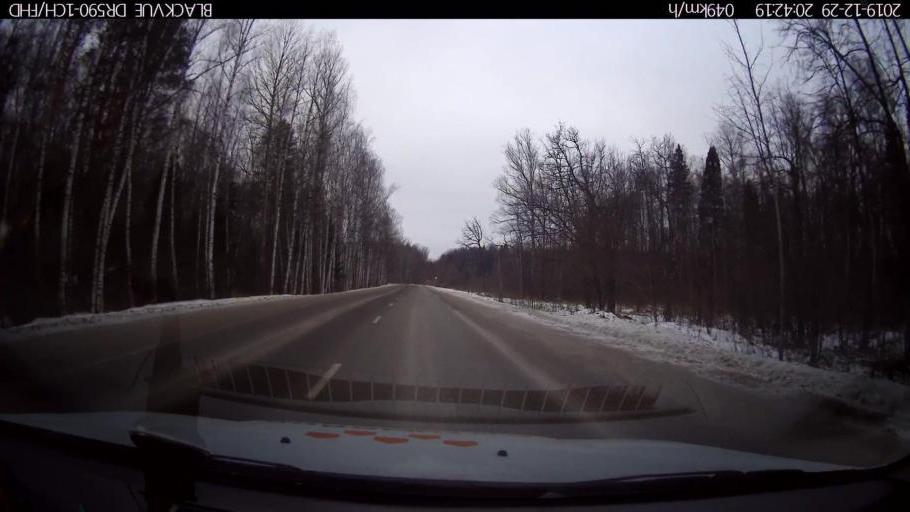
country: RU
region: Nizjnij Novgorod
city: Afonino
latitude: 56.1904
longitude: 44.0299
